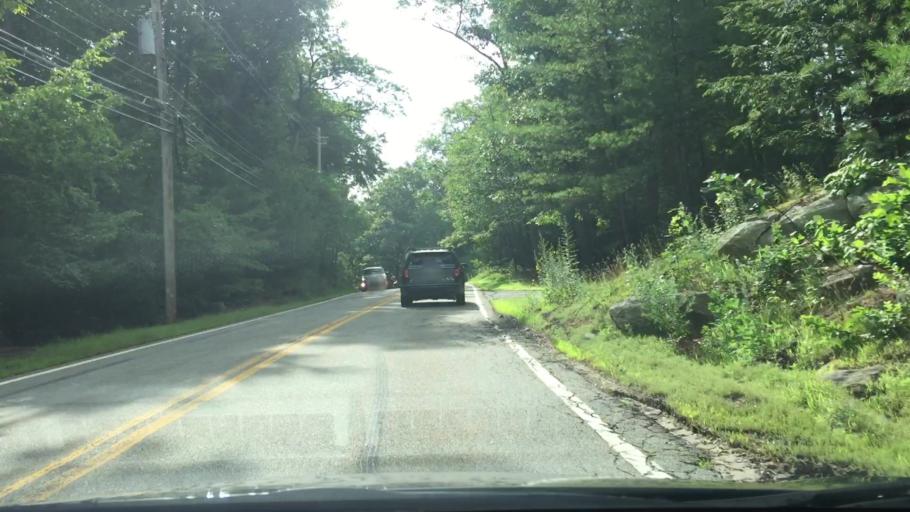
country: US
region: Massachusetts
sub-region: Middlesex County
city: Stow
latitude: 42.4825
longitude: -71.5196
